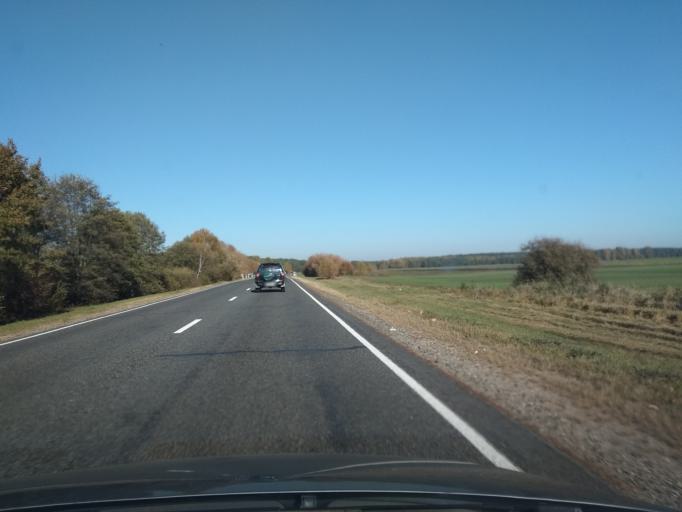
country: BY
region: Brest
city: Kobryn
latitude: 52.1250
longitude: 24.3052
